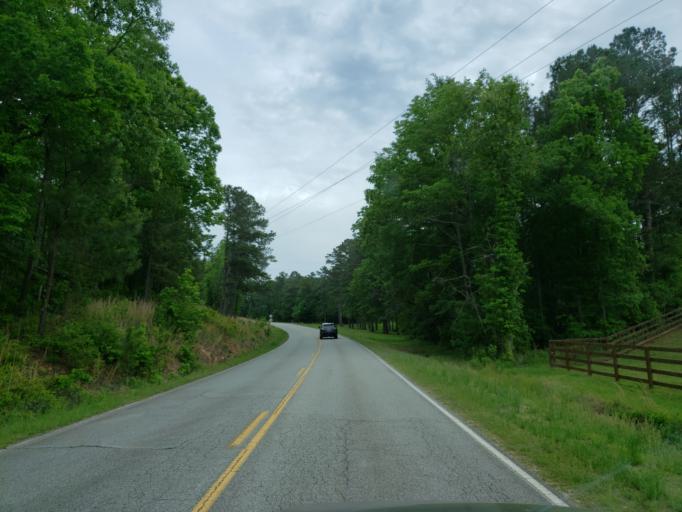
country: US
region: Georgia
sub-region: Bibb County
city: West Point
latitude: 32.8169
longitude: -83.8572
